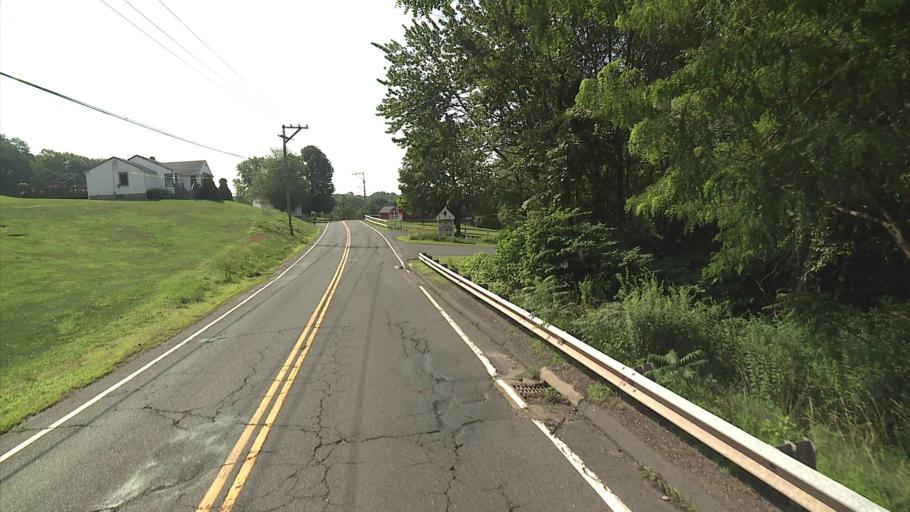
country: US
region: Connecticut
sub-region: New Haven County
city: Wolcott
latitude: 41.5982
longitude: -72.9655
